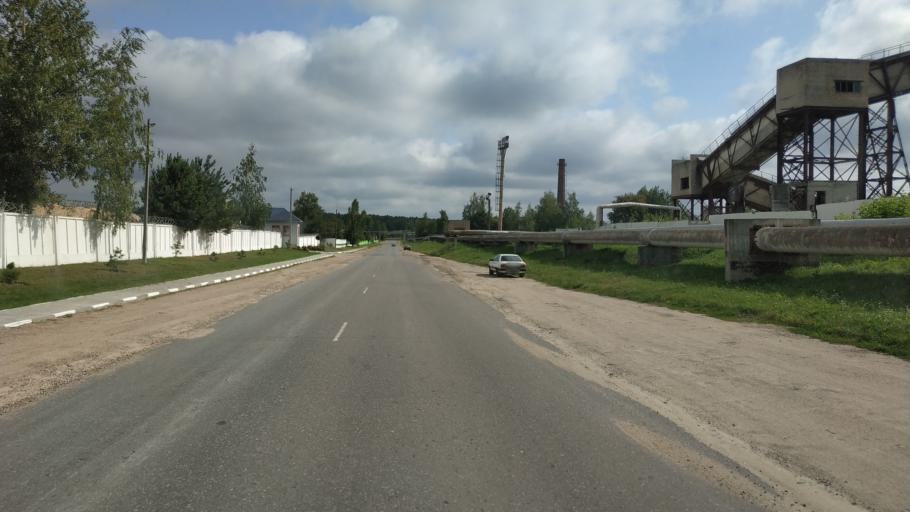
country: BY
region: Mogilev
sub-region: Mahilyowski Rayon
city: Veyno
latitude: 53.8413
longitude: 30.3791
